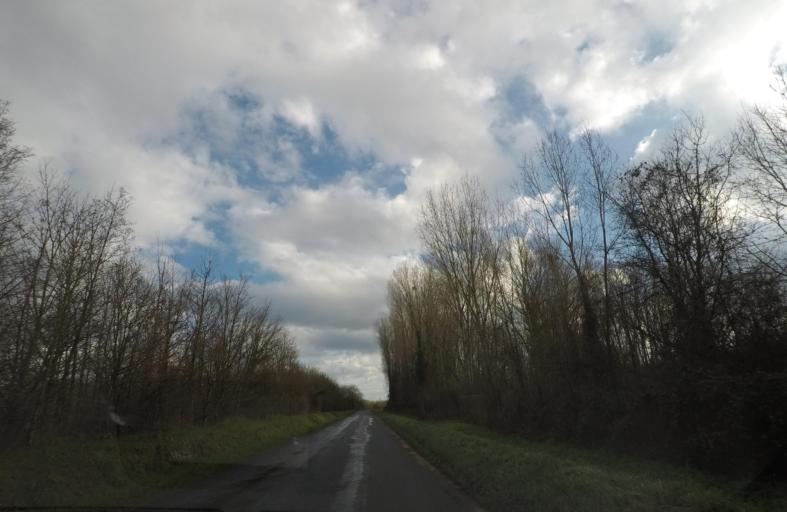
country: FR
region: Centre
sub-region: Departement du Cher
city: Bourges
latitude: 47.0489
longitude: 2.4134
